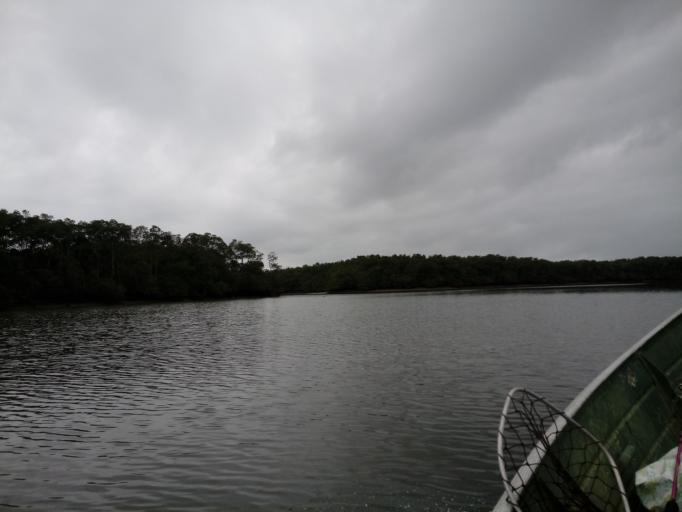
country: BR
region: Sao Paulo
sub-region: Cananeia
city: Cananeia
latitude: -24.8829
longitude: -47.8033
